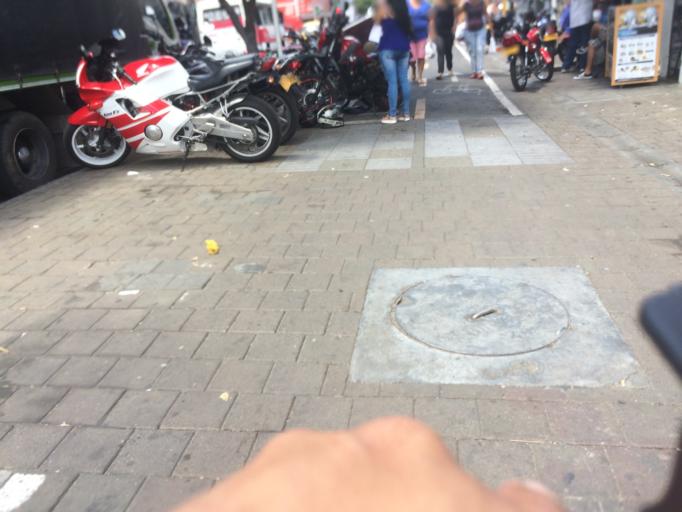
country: CO
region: Antioquia
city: Medellin
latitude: 6.2579
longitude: -75.5676
